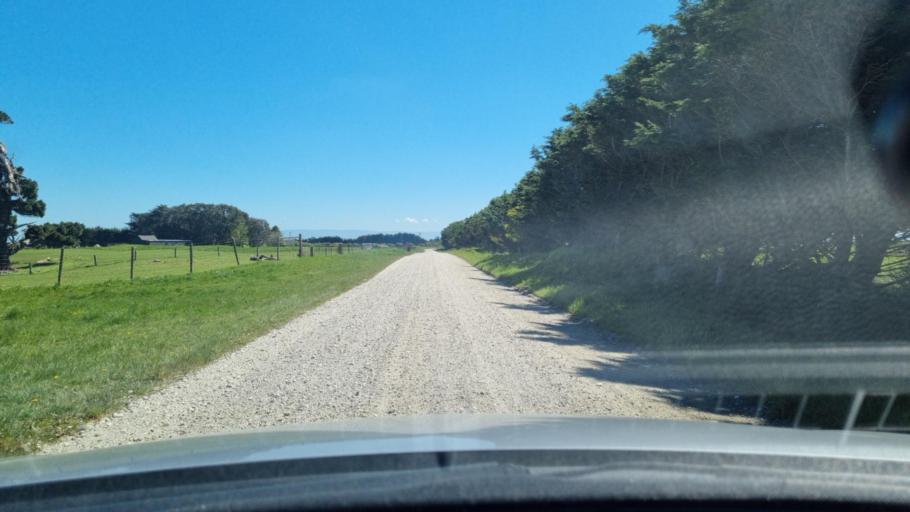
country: NZ
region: Southland
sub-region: Invercargill City
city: Invercargill
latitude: -46.4175
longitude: 168.2675
